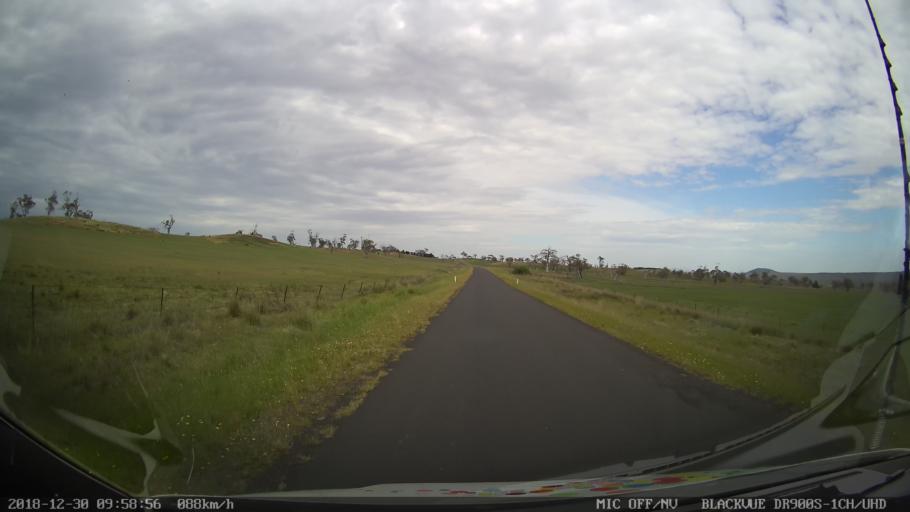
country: AU
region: New South Wales
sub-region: Cooma-Monaro
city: Cooma
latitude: -36.5224
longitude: 149.2184
